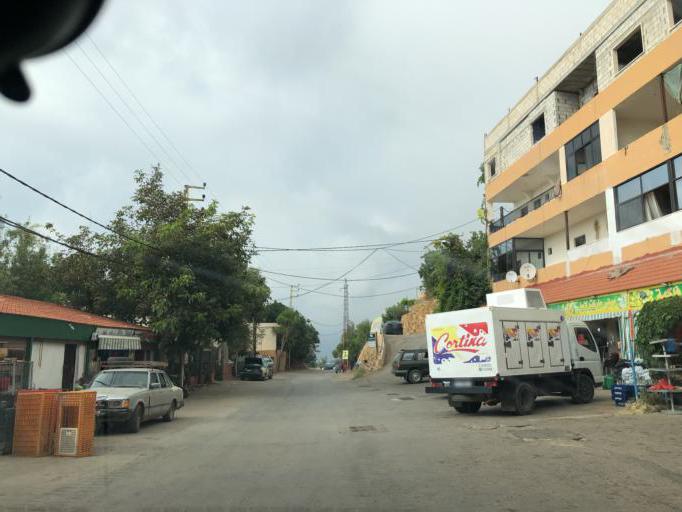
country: LB
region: Mont-Liban
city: Jbail
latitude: 34.0694
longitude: 35.8540
